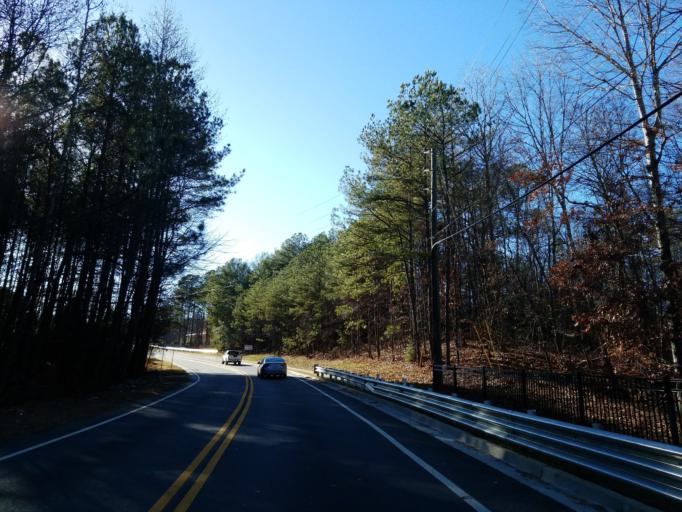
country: US
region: Georgia
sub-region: Cobb County
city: Mableton
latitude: 33.7772
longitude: -84.5596
